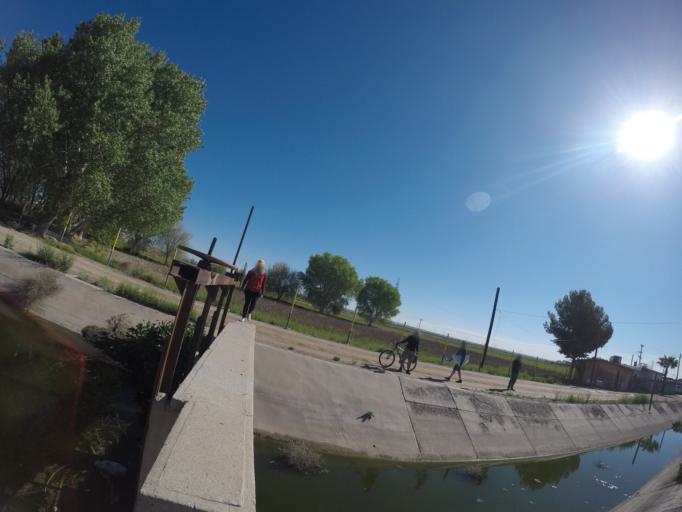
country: US
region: Texas
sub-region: El Paso County
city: Socorro
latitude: 31.6460
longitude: -106.3390
